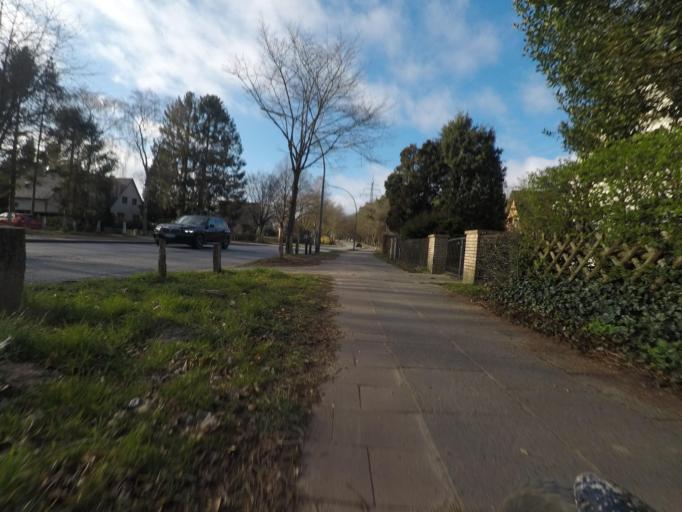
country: DE
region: Hamburg
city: Sasel
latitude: 53.6337
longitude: 10.1040
